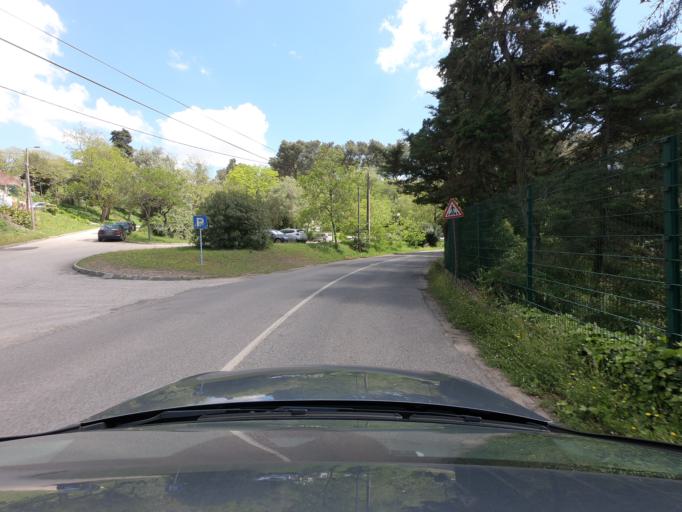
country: PT
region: Lisbon
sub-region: Oeiras
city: Linda-a-Velha
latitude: 38.7084
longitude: -9.2518
